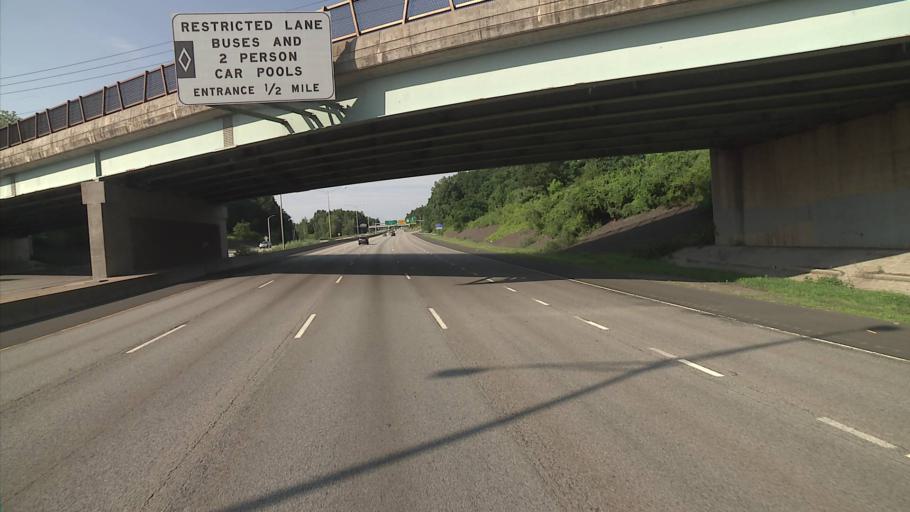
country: US
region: Connecticut
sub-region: Hartford County
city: Windsor Locks
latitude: 41.9047
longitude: -72.6348
